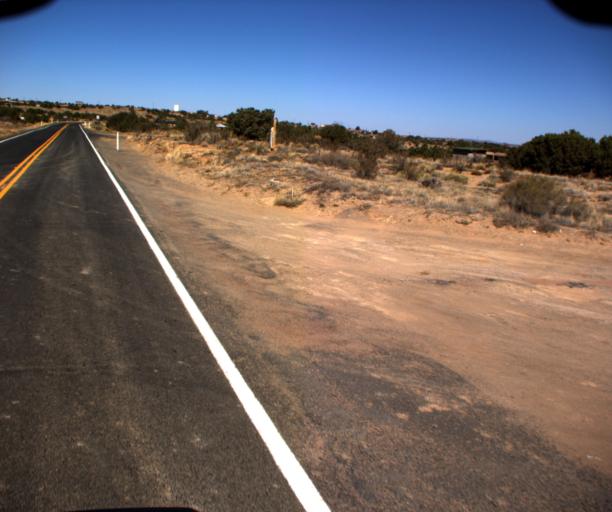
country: US
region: Arizona
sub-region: Navajo County
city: First Mesa
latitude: 35.9035
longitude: -110.6659
